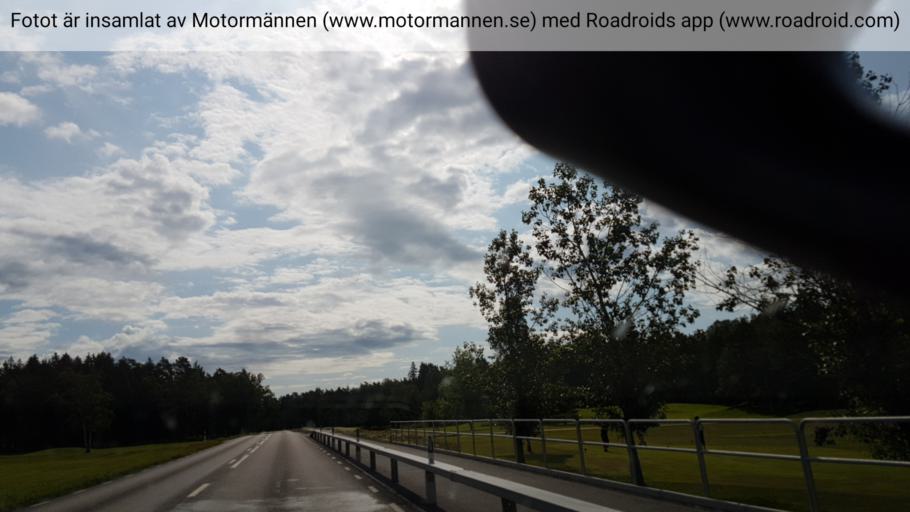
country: SE
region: Vaestra Goetaland
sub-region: Grastorps Kommun
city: Graestorp
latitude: 58.3352
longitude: 12.6545
